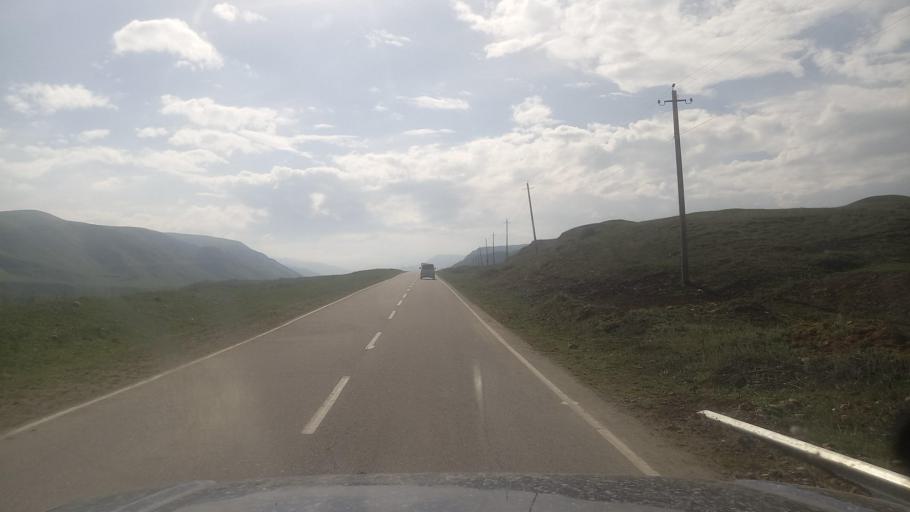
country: RU
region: Kabardino-Balkariya
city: Kamennomostskoye
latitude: 43.7359
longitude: 42.9985
